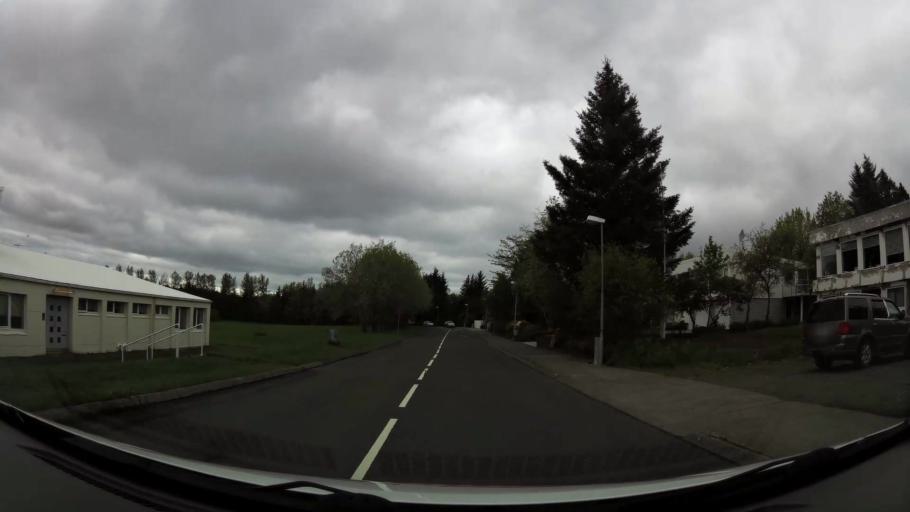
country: IS
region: Capital Region
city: Reykjavik
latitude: 64.1391
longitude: -21.8618
